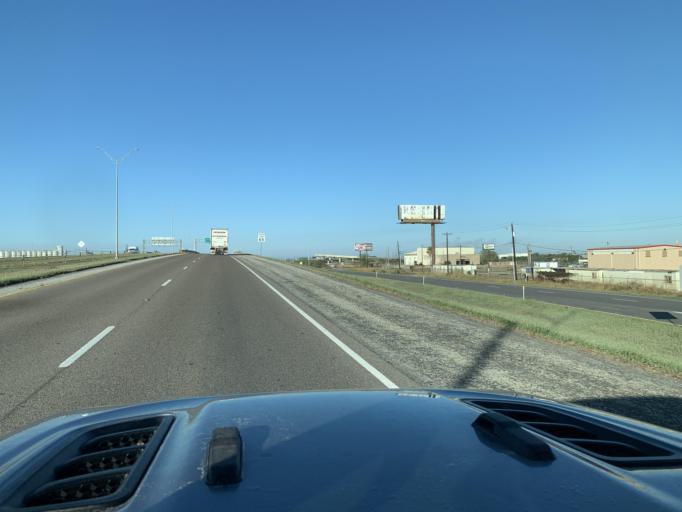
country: US
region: Texas
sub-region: Nueces County
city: Corpus Christi
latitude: 27.7820
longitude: -97.4755
